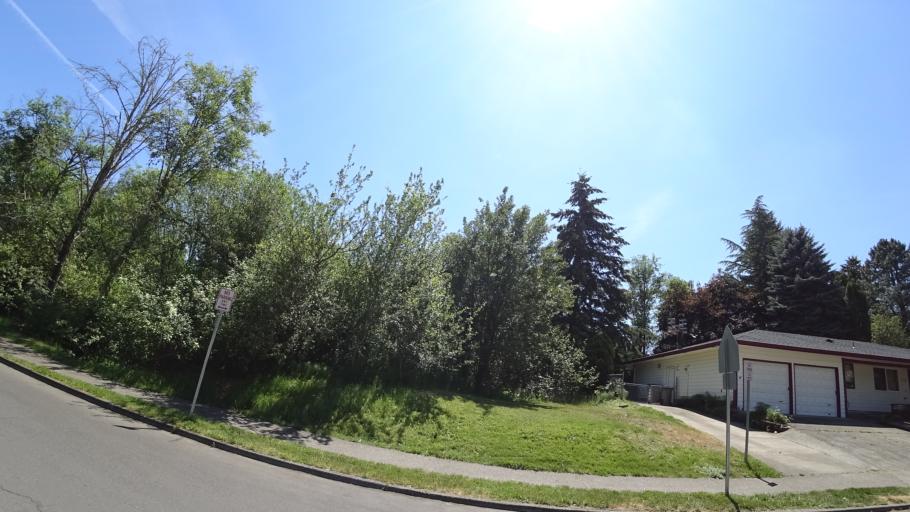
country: US
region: Oregon
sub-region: Washington County
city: King City
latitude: 45.4329
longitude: -122.8027
